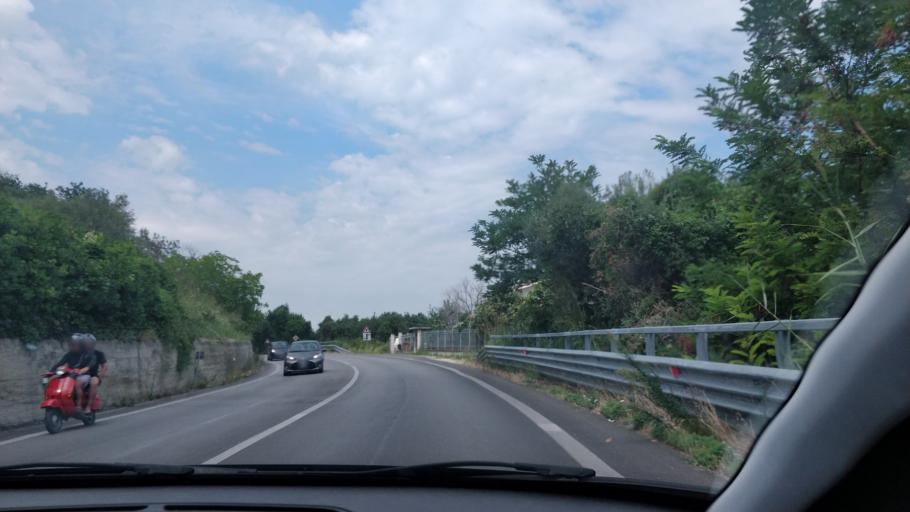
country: IT
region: Abruzzo
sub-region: Provincia di Chieti
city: Marina di San Vito
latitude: 42.3190
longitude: 14.4328
